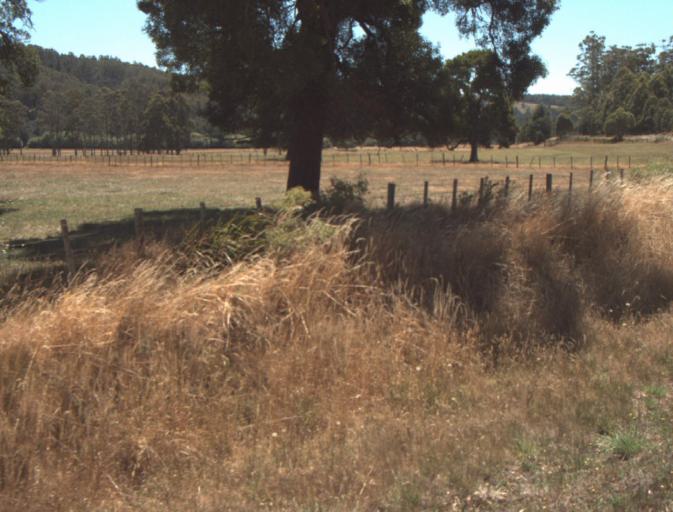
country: AU
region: Tasmania
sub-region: Launceston
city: Newstead
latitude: -41.3231
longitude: 147.3619
